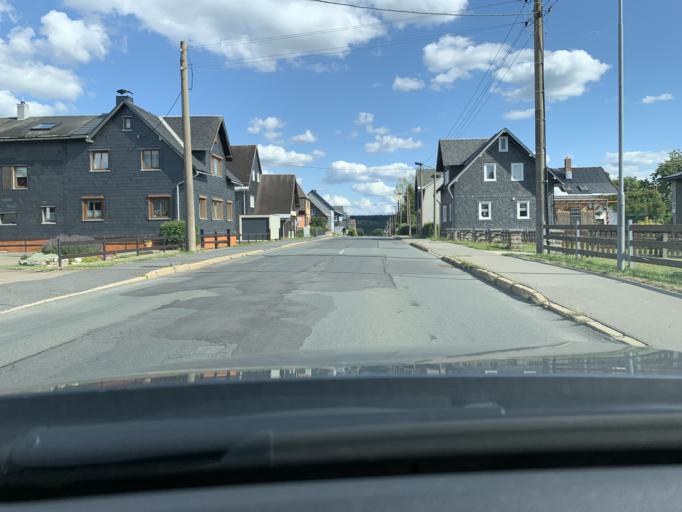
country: DE
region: Thuringia
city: Lauscha
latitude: 50.4964
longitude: 11.1551
